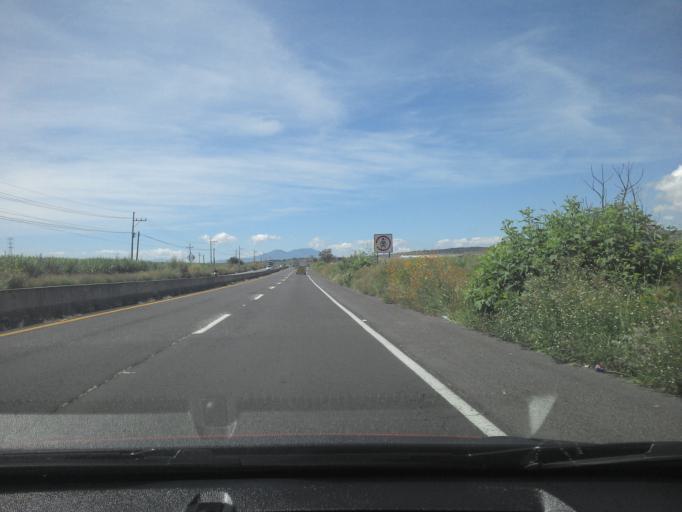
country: MX
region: Jalisco
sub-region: Tala
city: Los Ruisenores
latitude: 20.7073
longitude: -103.6774
